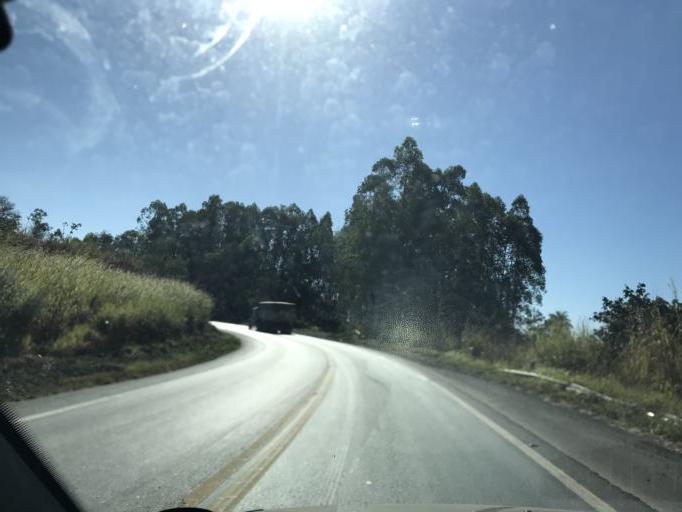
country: BR
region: Minas Gerais
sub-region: Bambui
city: Bambui
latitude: -19.8559
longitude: -45.9868
